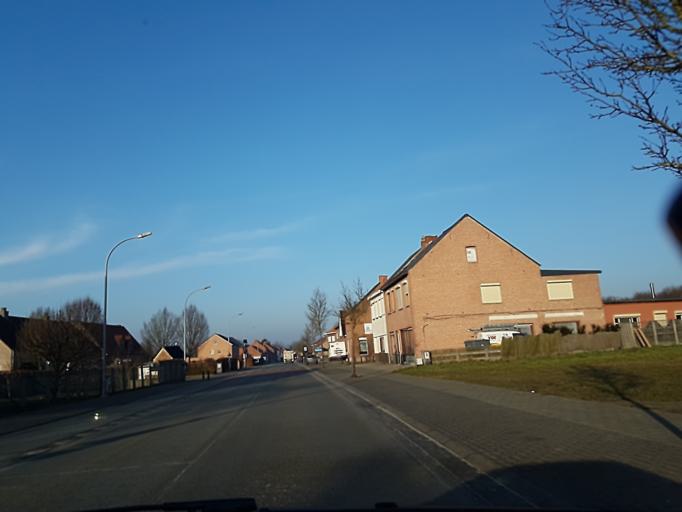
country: BE
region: Flanders
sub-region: Provincie Vlaams-Brabant
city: Tremelo
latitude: 51.0136
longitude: 4.7101
